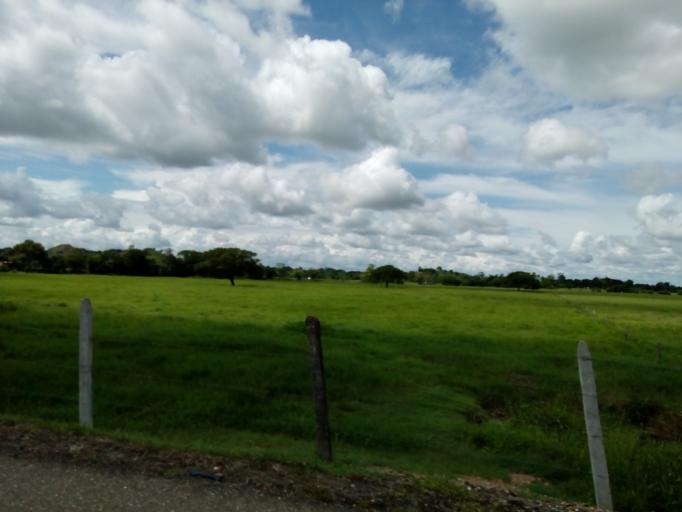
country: CO
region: Boyaca
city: Puerto Boyaca
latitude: 5.9396
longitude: -74.5675
